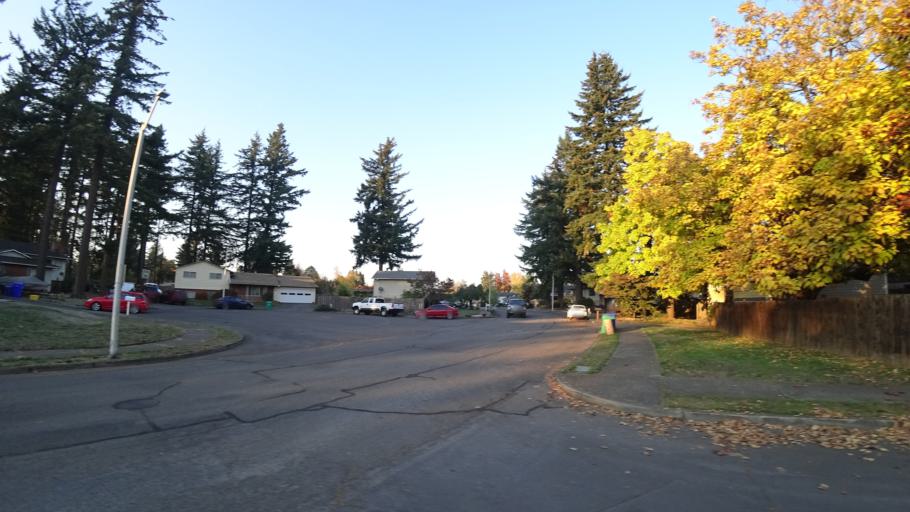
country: US
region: Oregon
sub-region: Multnomah County
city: Gresham
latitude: 45.5156
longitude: -122.4509
